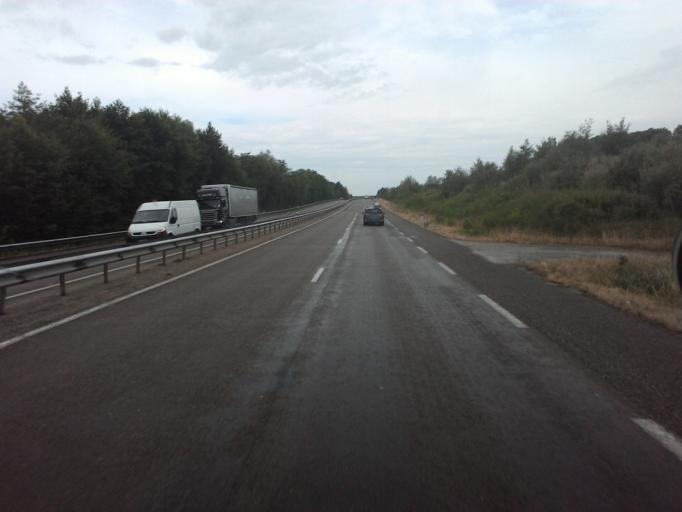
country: FR
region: Franche-Comte
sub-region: Departement du Jura
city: Poligny
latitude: 46.8417
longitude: 5.6652
